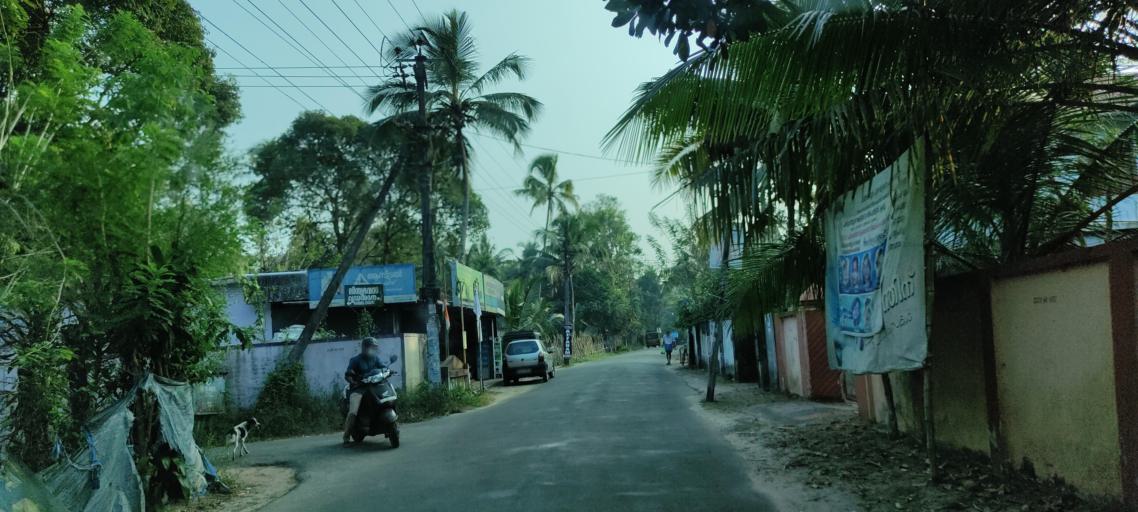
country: IN
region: Kerala
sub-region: Alappuzha
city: Shertallai
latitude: 9.6653
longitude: 76.3535
